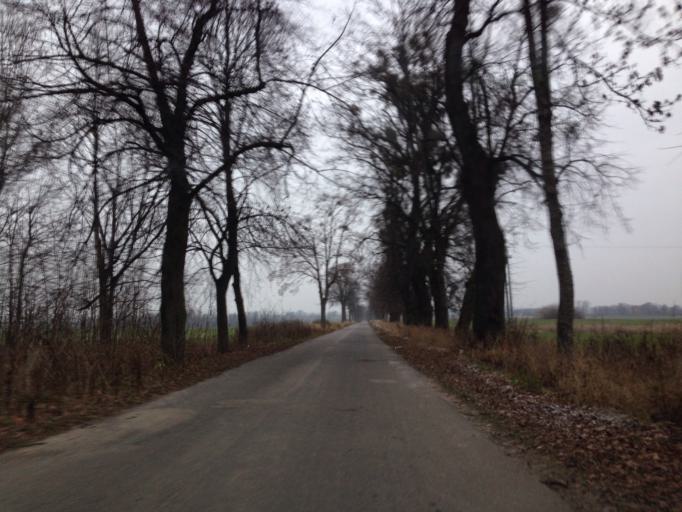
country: PL
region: Warmian-Masurian Voivodeship
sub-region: Powiat ketrzynski
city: Reszel
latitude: 54.1110
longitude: 21.2263
